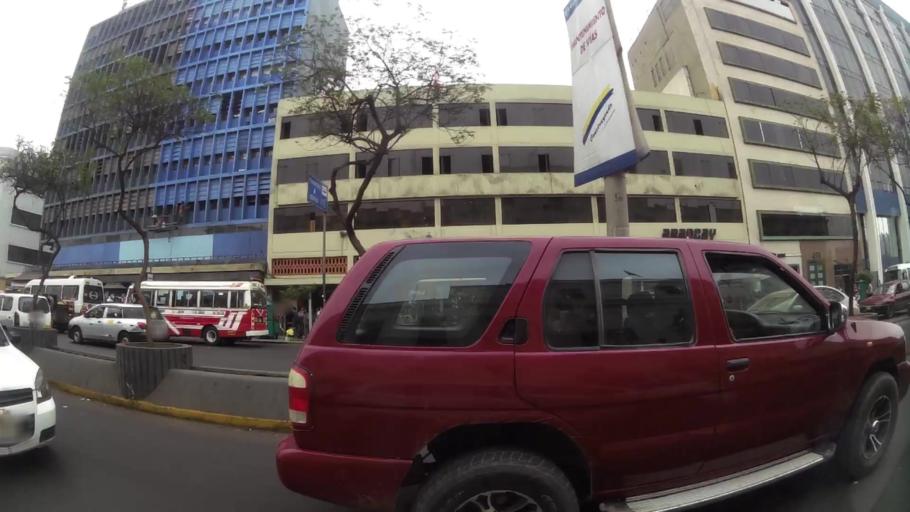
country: PE
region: Lima
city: Lima
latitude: -12.0501
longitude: -77.0280
